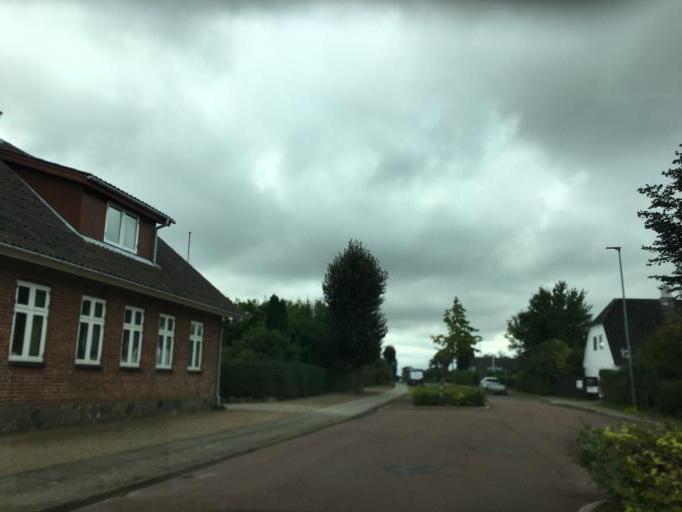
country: DK
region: South Denmark
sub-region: Kolding Kommune
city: Kolding
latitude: 55.5876
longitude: 9.4922
